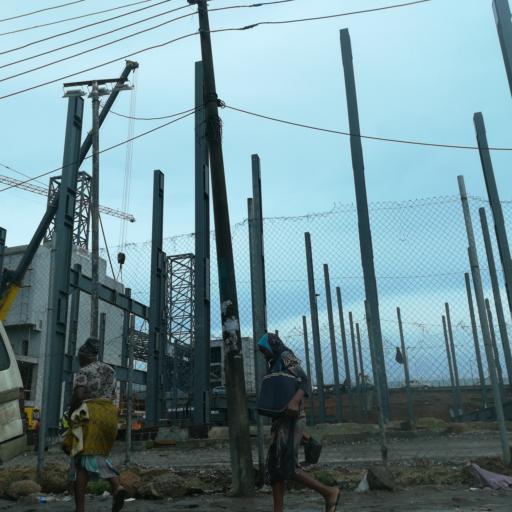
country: NG
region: Lagos
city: Oshodi
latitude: 6.5562
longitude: 3.3506
